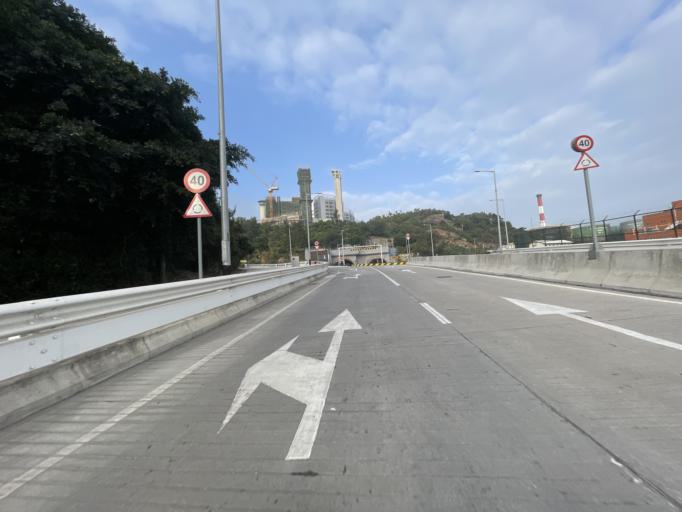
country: MO
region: Macau
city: Macau
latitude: 22.1351
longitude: 113.5805
